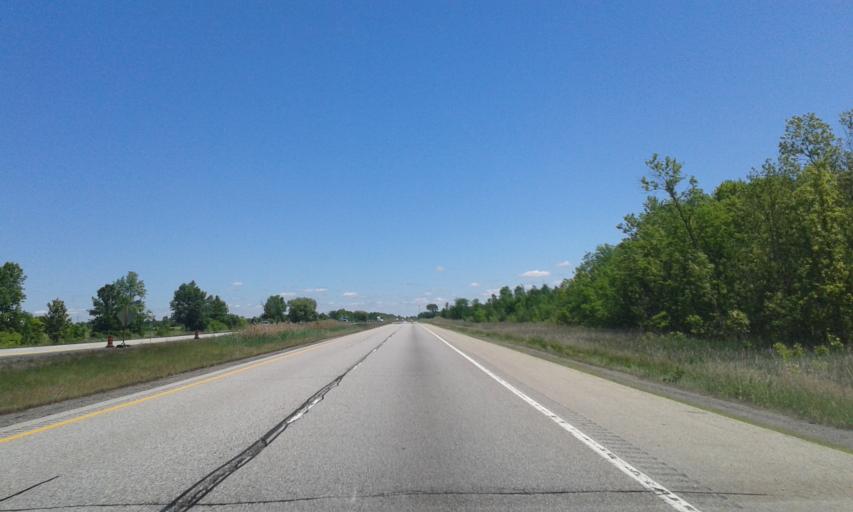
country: US
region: New York
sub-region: St. Lawrence County
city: Ogdensburg
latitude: 44.8721
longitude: -75.3015
